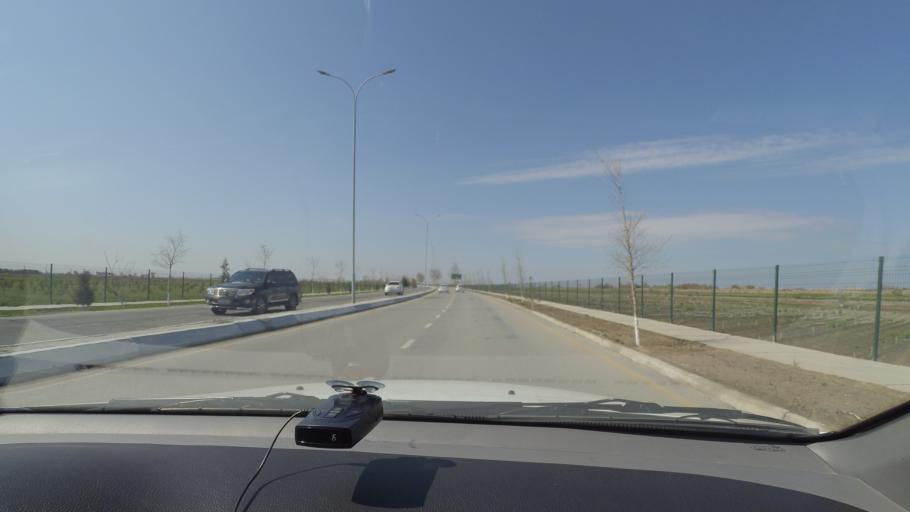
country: UZ
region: Bukhara
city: Galaosiyo
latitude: 39.8039
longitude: 64.4965
